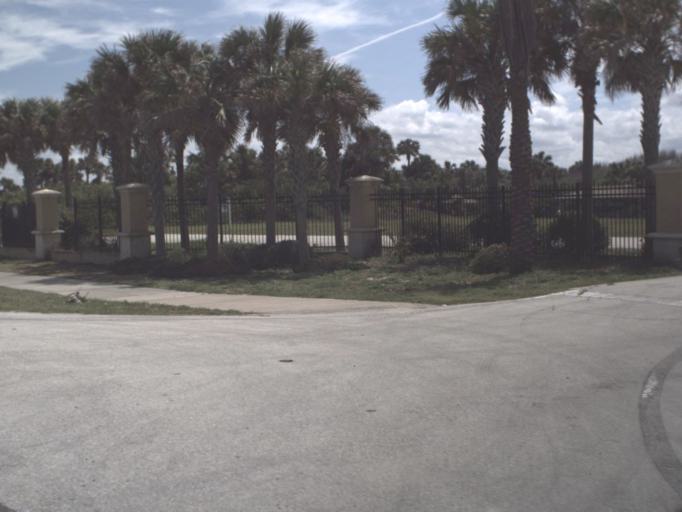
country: US
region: Florida
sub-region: Flagler County
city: Palm Coast
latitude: 29.5480
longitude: -81.1610
